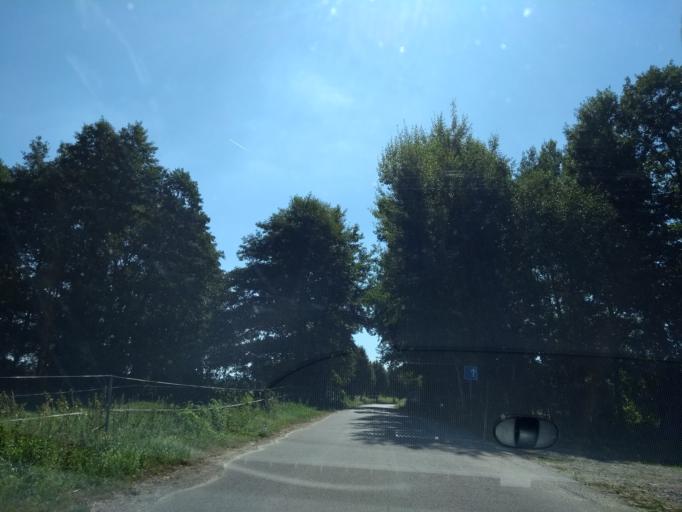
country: DE
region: Brandenburg
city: Lubbenau
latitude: 51.8320
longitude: 13.9521
